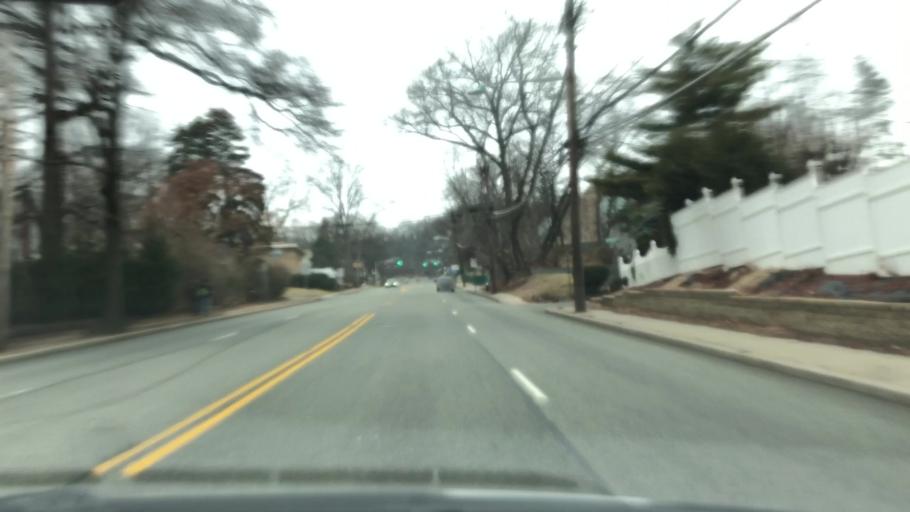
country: US
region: New Jersey
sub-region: Essex County
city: Orange
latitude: 40.7763
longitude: -74.2502
